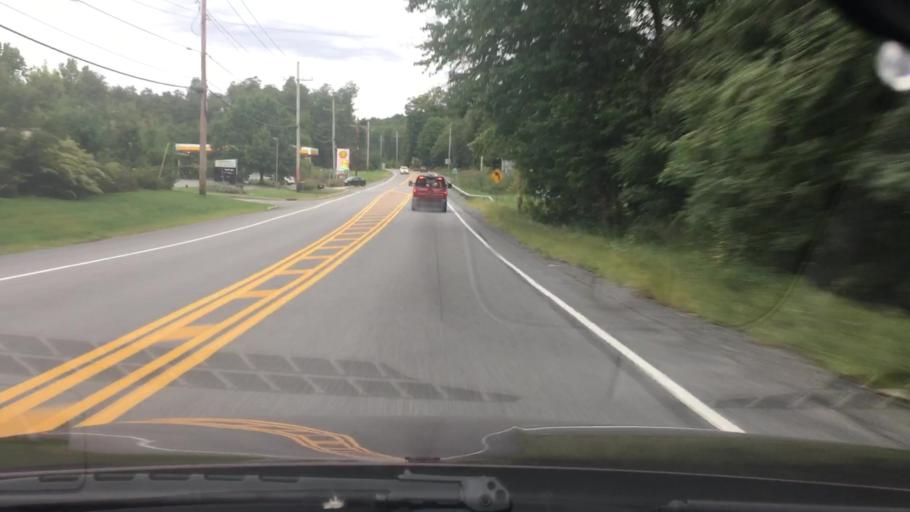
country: US
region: New York
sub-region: Dutchess County
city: Pleasant Valley
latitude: 41.7796
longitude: -73.7647
